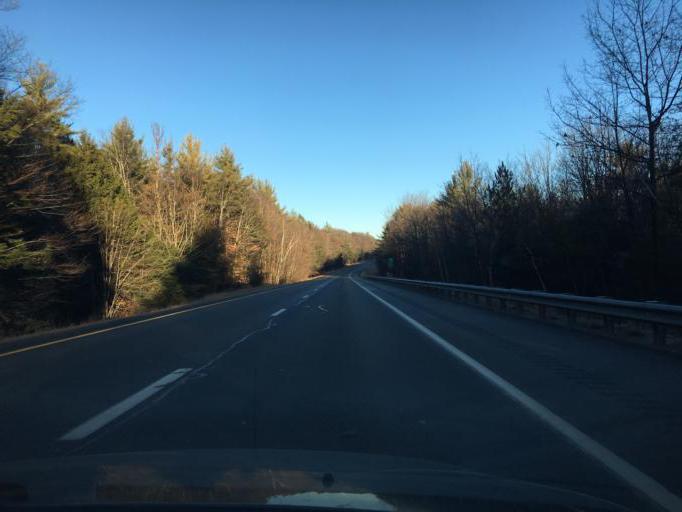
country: US
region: New Hampshire
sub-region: Belknap County
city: Sanbornton
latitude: 43.4826
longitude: -71.5906
